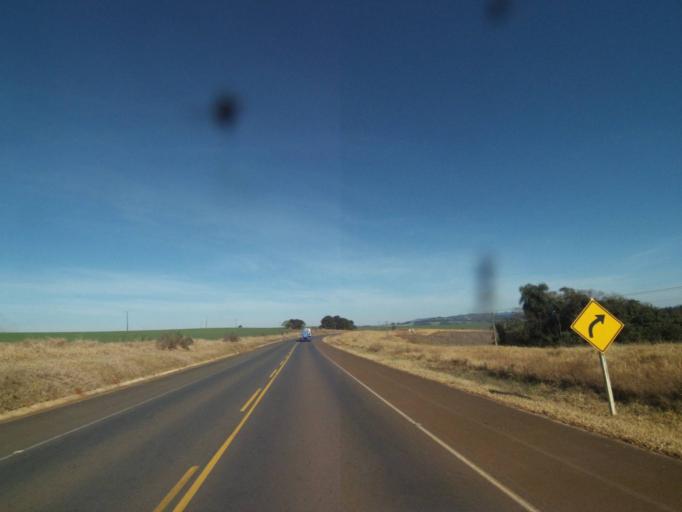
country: BR
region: Parana
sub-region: Tibagi
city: Tibagi
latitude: -24.4544
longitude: -50.4237
